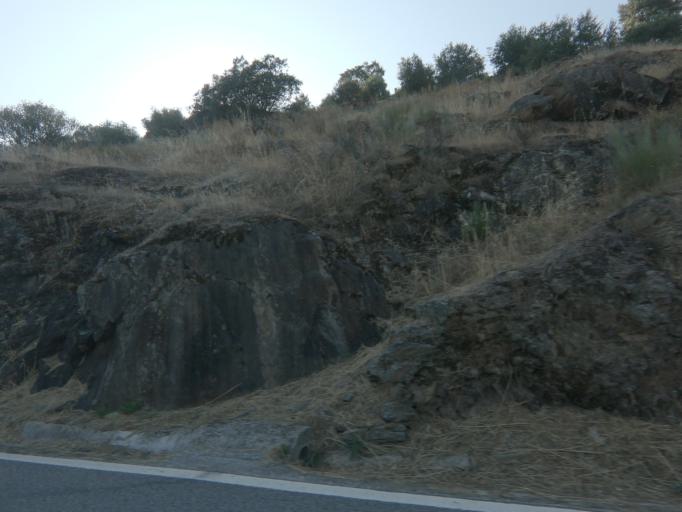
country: PT
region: Viseu
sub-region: Tabuaco
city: Tabuaco
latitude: 41.1383
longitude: -7.5644
